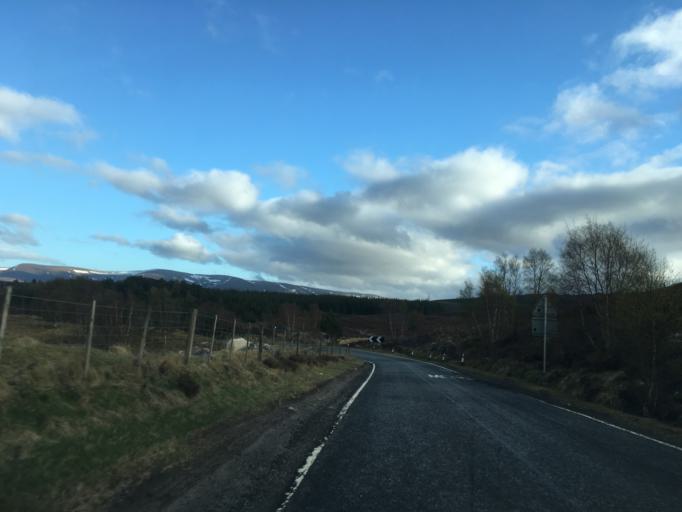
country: GB
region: Scotland
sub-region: Highland
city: Kingussie
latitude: 56.9919
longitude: -4.2496
